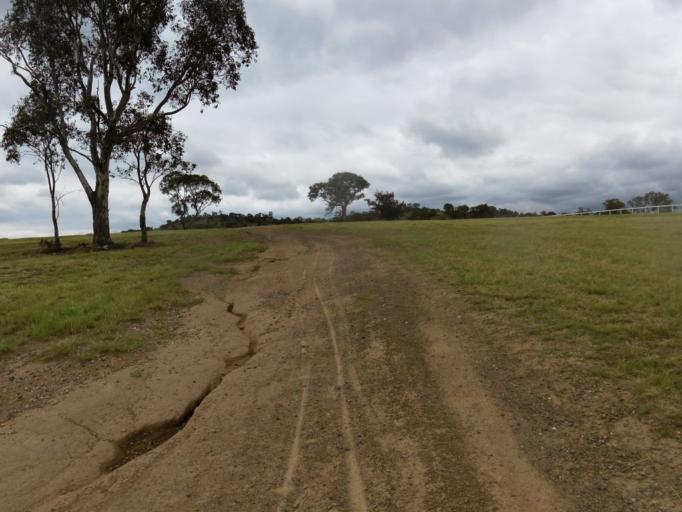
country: AU
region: Australian Capital Territory
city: Macquarie
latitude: -35.3444
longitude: 149.0272
